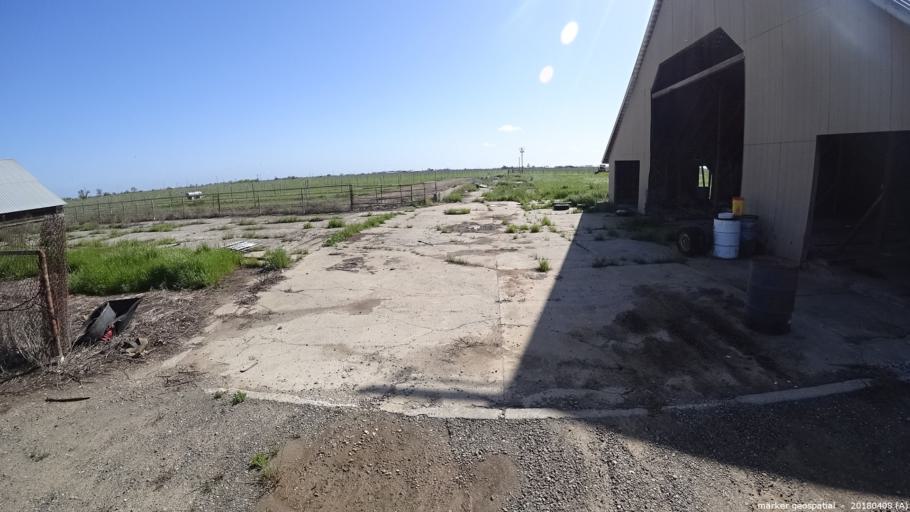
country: US
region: California
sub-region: Sacramento County
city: Laguna
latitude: 38.3460
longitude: -121.4640
